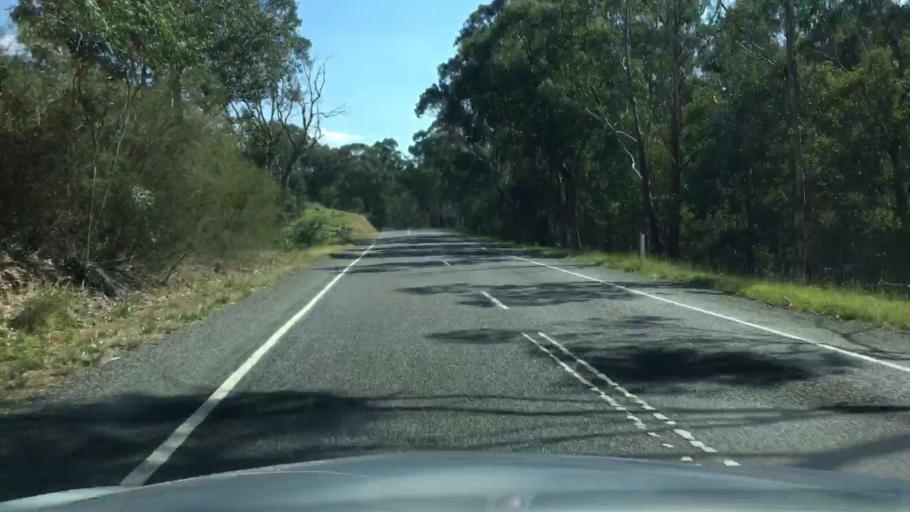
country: AU
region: Victoria
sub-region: Nillumbik
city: Saint Andrews
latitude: -37.6571
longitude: 145.2743
